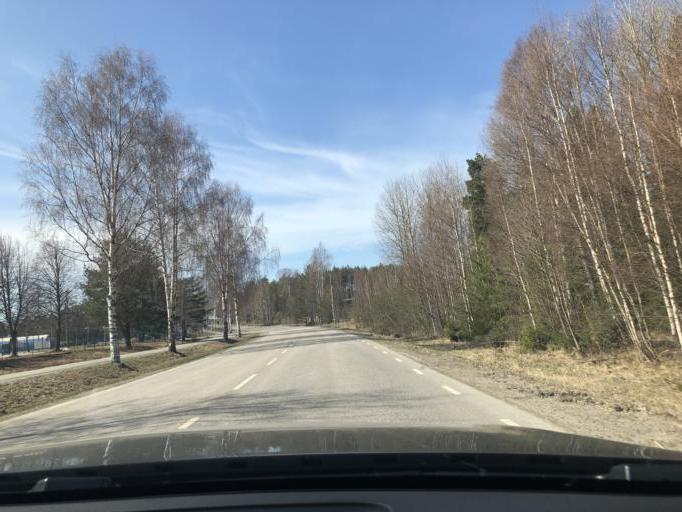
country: SE
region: Gaevleborg
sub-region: Hudiksvalls Kommun
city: Hudiksvall
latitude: 61.7249
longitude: 17.1529
